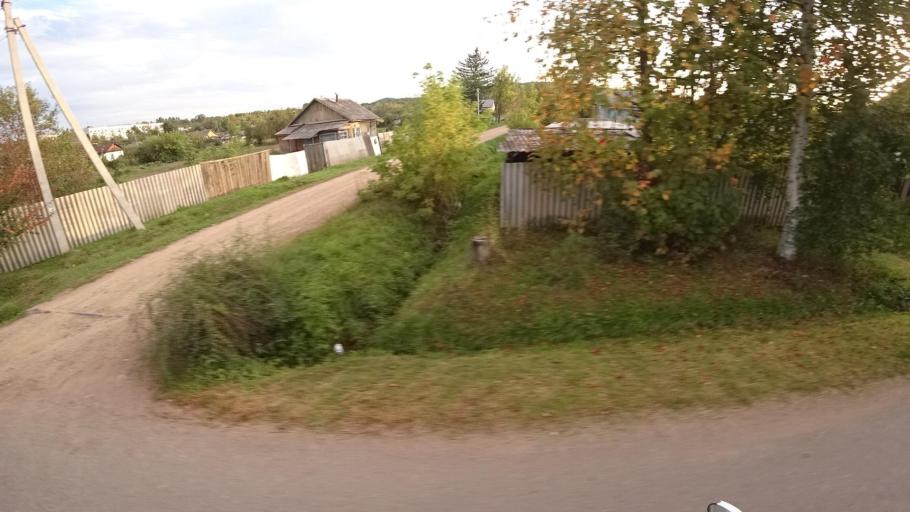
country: RU
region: Primorskiy
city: Yakovlevka
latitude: 44.4216
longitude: 133.4733
